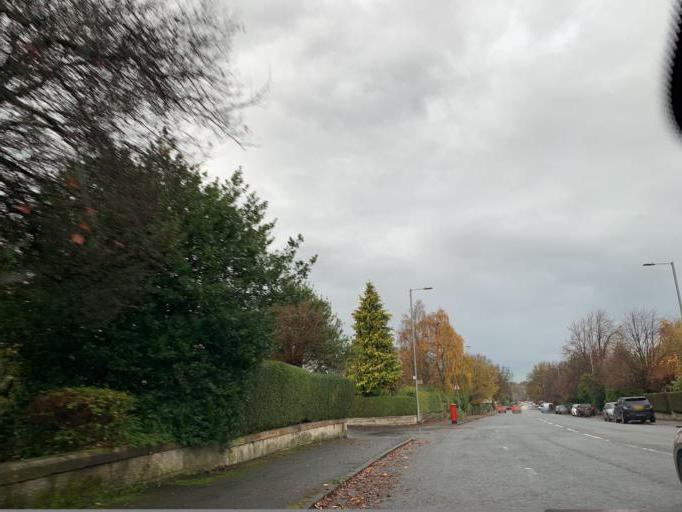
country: GB
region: Scotland
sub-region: East Renfrewshire
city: Giffnock
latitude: 55.8154
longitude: -4.2857
